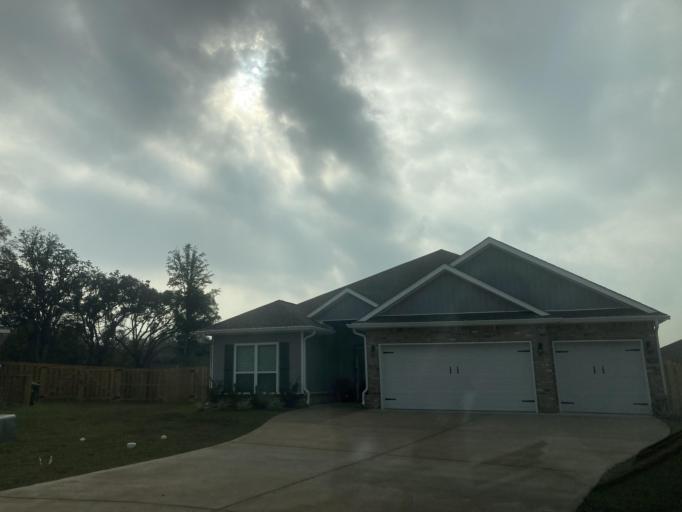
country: US
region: Mississippi
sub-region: Harrison County
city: Long Beach
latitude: 30.3753
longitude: -89.1583
